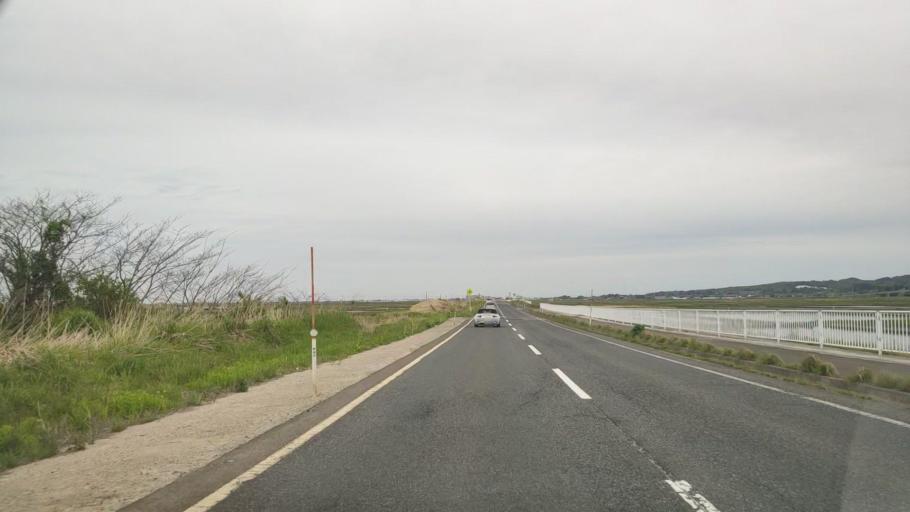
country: JP
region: Niigata
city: Niitsu-honcho
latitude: 37.7597
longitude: 139.0942
